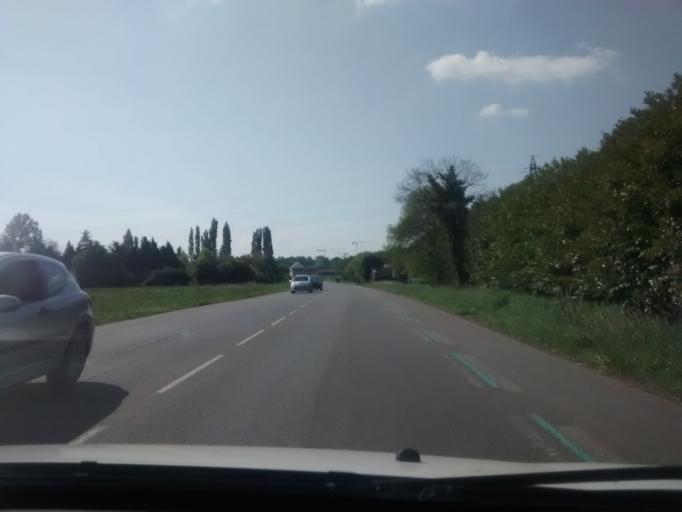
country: FR
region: Brittany
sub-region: Departement d'Ille-et-Vilaine
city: Montgermont
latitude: 48.1452
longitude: -1.7029
